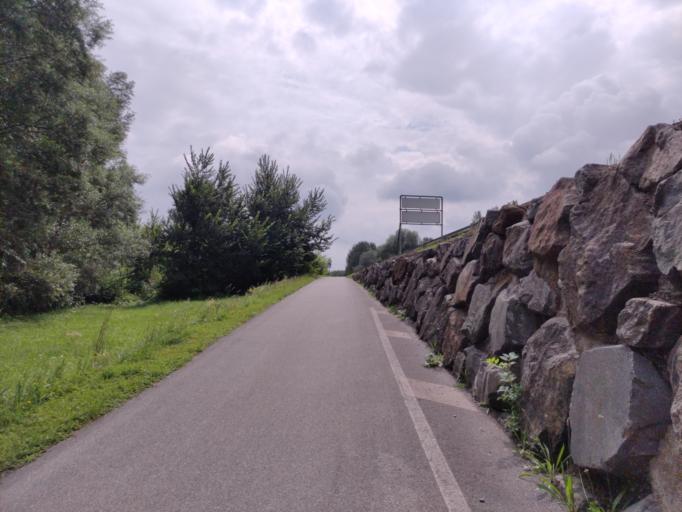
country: AT
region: Lower Austria
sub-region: Politischer Bezirk Melk
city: Ybbs an der Donau
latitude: 48.1650
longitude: 15.0926
